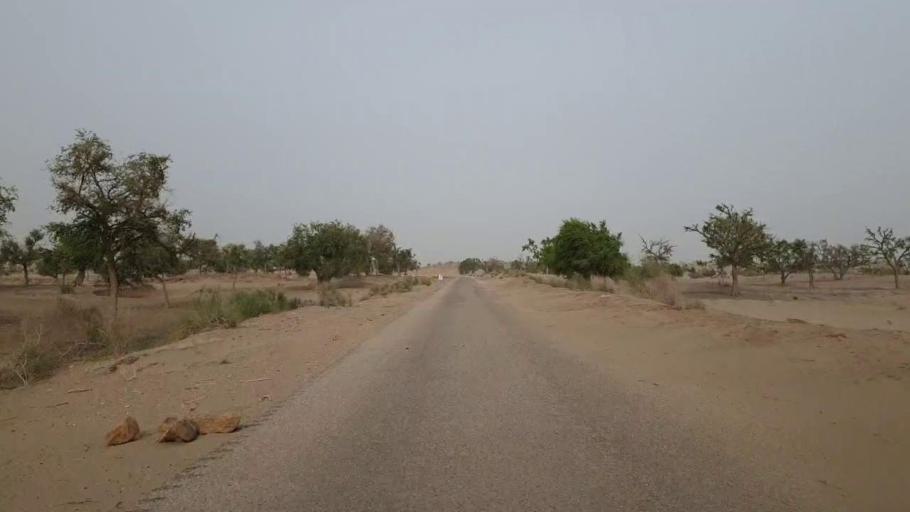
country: PK
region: Sindh
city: Islamkot
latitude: 24.5444
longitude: 70.3768
